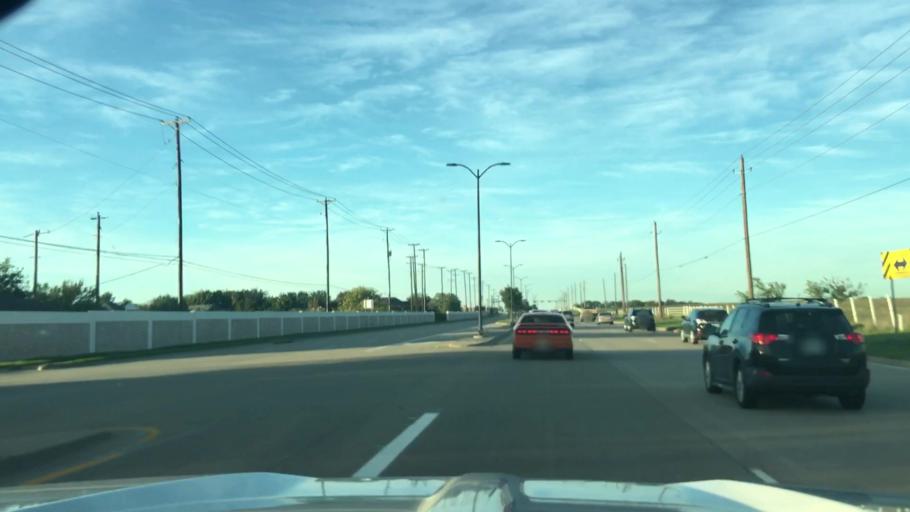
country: US
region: Texas
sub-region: Collin County
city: Frisco
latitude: 33.1594
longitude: -96.8032
